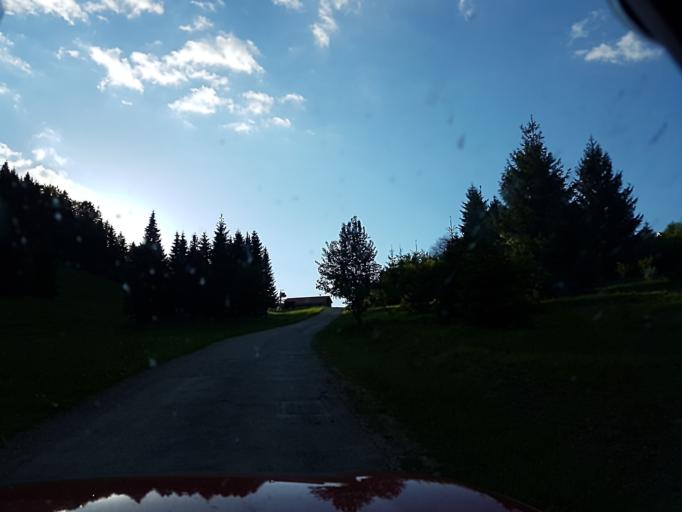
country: SK
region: Zilinsky
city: Ruzomberok
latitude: 49.0501
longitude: 19.2670
